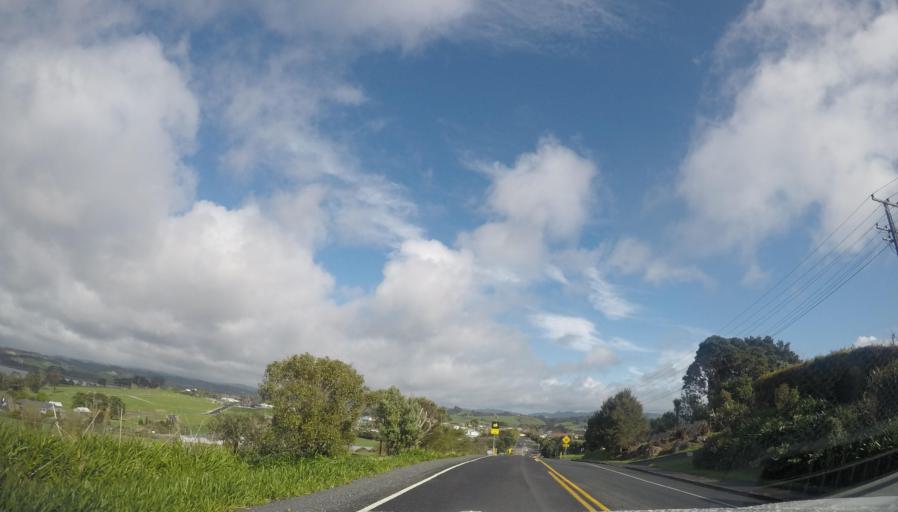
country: NZ
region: Auckland
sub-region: Auckland
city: Warkworth
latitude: -36.4284
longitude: 174.7330
